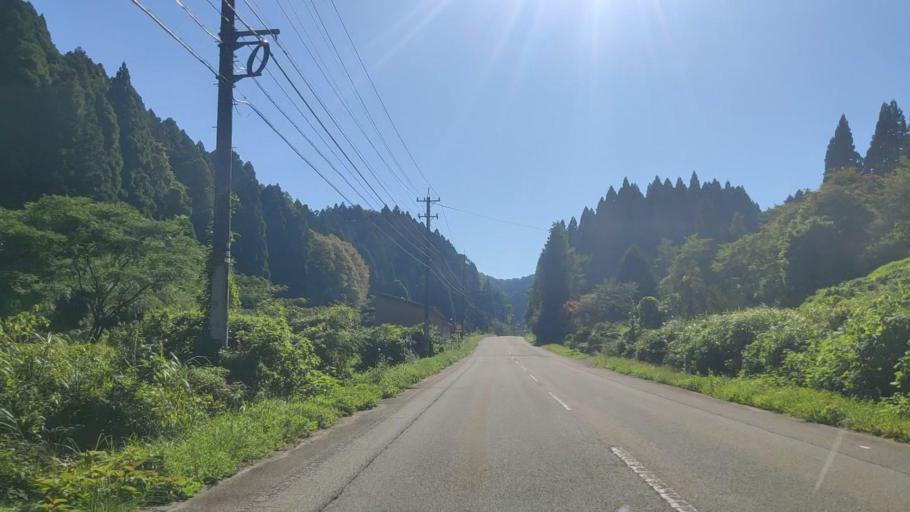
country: JP
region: Ishikawa
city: Nanao
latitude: 37.3255
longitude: 137.1938
